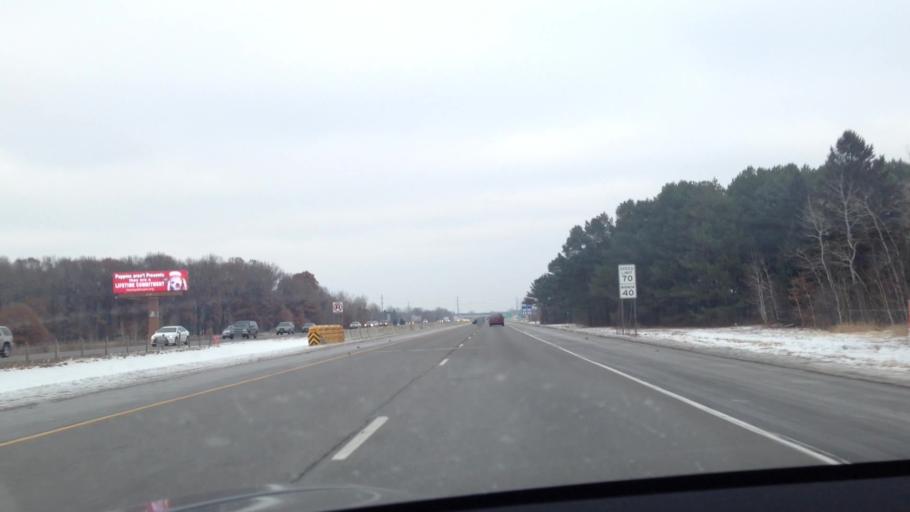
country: US
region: Minnesota
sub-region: Anoka County
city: Lexington
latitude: 45.1495
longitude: -93.1768
